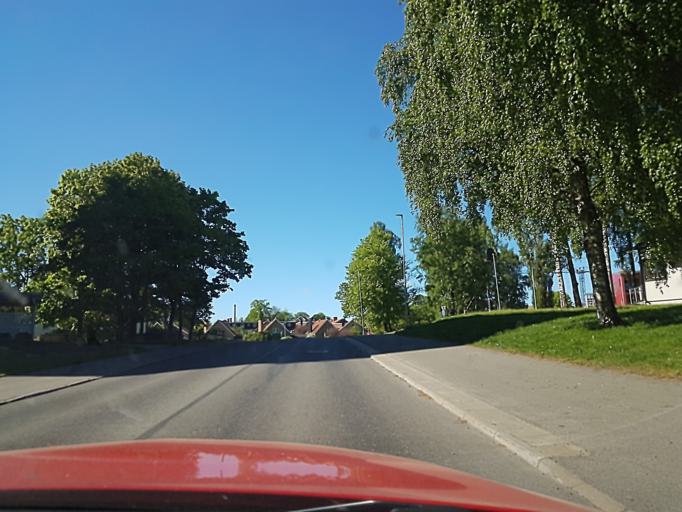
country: SE
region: Vaestra Goetaland
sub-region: Skovde Kommun
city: Skoevde
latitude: 58.3903
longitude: 13.8631
